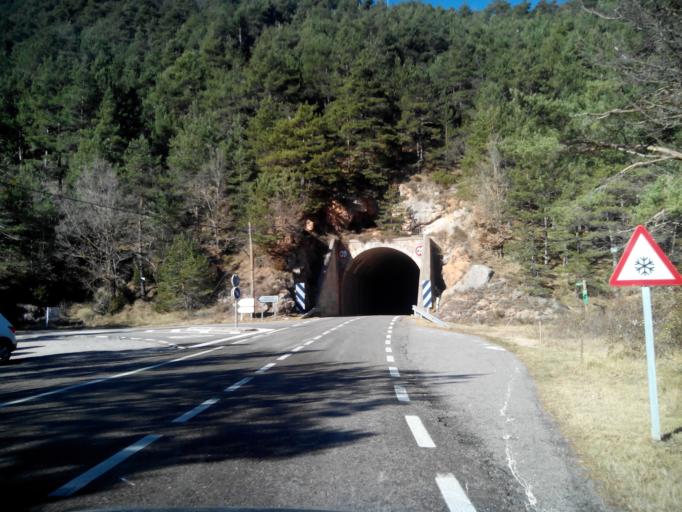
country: ES
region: Catalonia
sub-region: Provincia de Barcelona
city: Capolat
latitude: 42.0925
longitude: 1.7616
